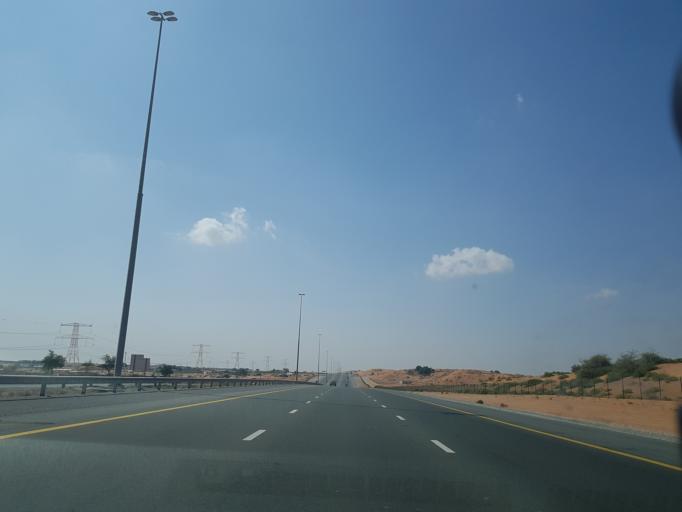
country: AE
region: Ra's al Khaymah
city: Ras al-Khaimah
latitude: 25.6903
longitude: 55.9184
